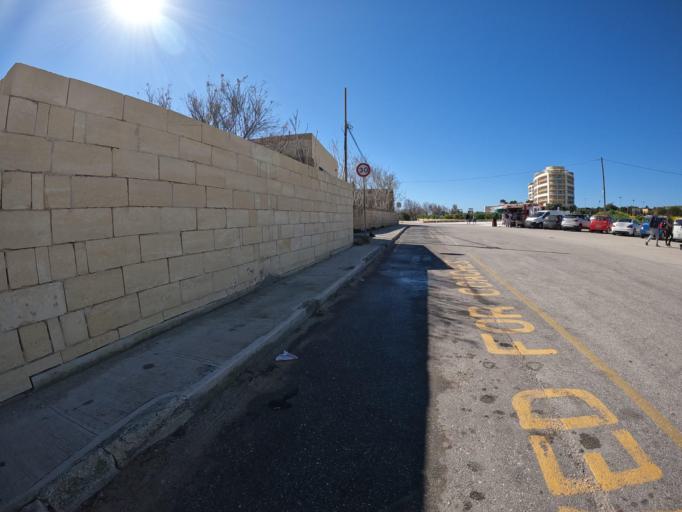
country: MT
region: L-Imgarr
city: Imgarr
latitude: 35.9354
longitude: 14.3470
